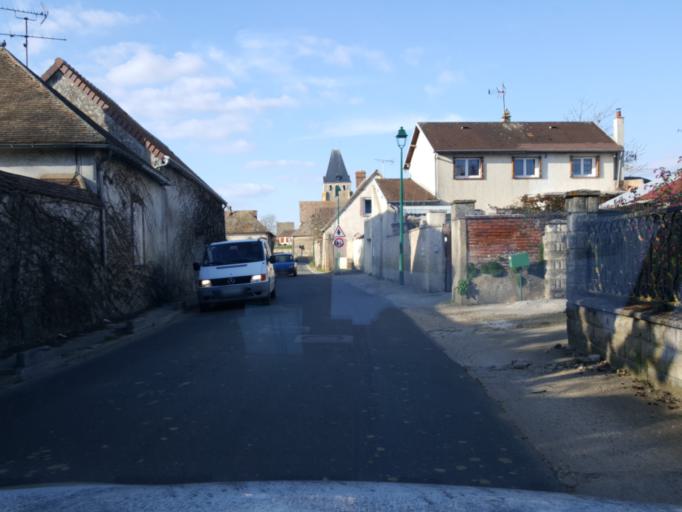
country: FR
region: Centre
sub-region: Departement d'Eure-et-Loir
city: Bu
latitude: 48.7459
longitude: 1.5229
